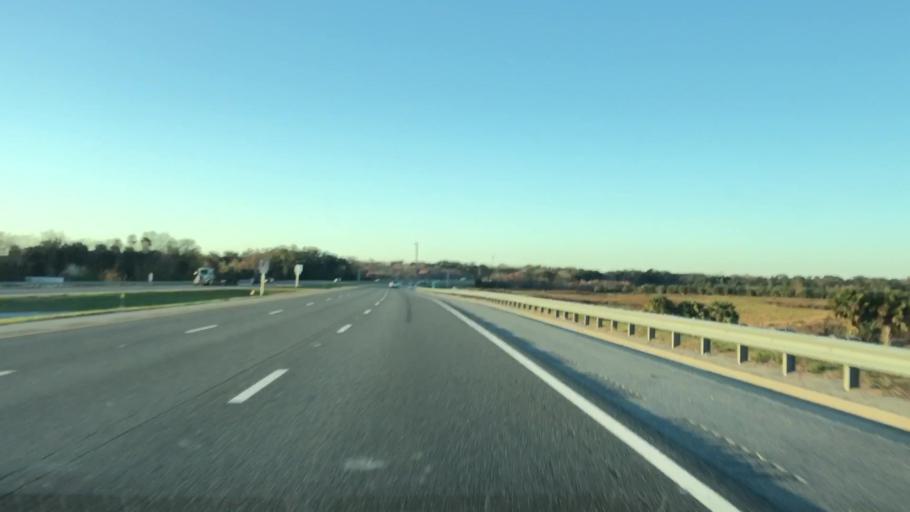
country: US
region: Florida
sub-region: Orange County
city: Apopka
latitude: 28.6705
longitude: -81.5560
